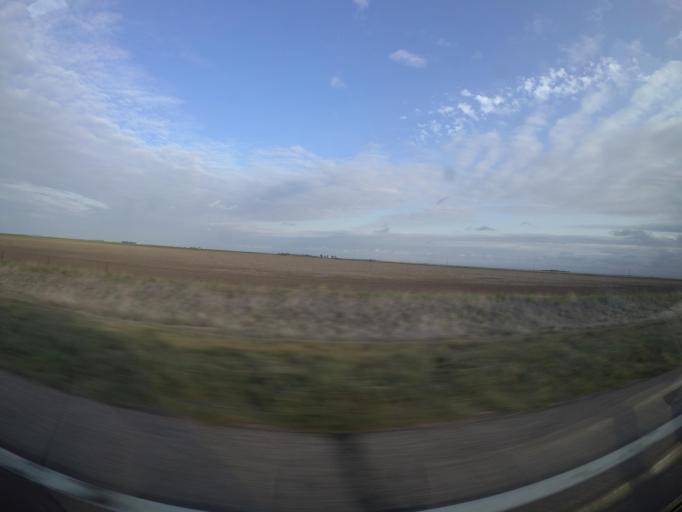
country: US
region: Colorado
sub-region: Kit Carson County
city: Burlington
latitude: 39.6747
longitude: -102.4171
